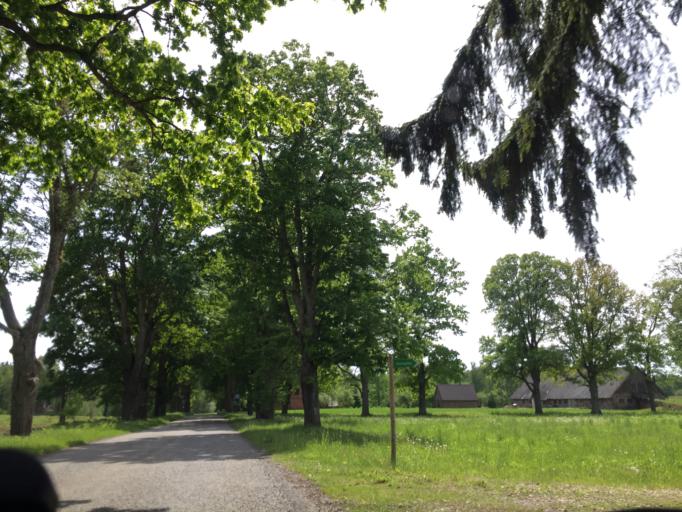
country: LV
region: Koceni
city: Koceni
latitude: 57.4878
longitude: 25.3644
